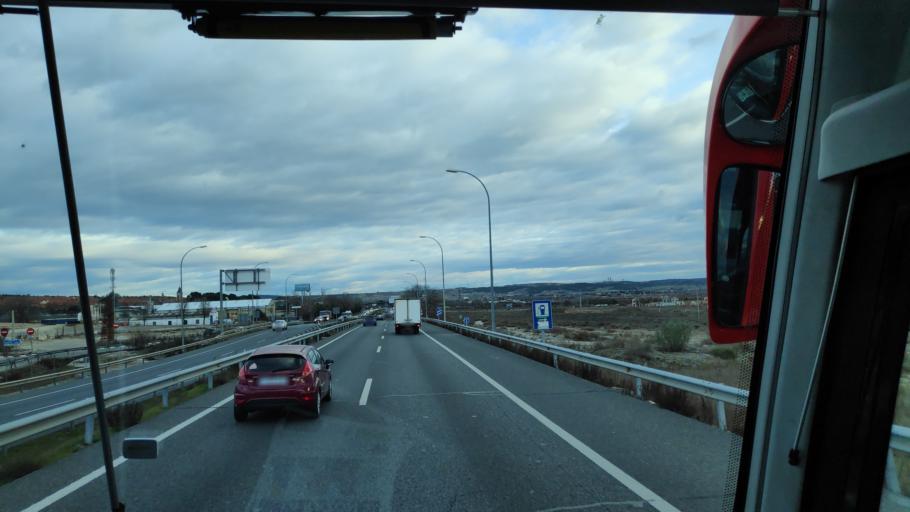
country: ES
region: Madrid
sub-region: Provincia de Madrid
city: Vaciamadrid
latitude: 40.3304
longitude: -3.5258
